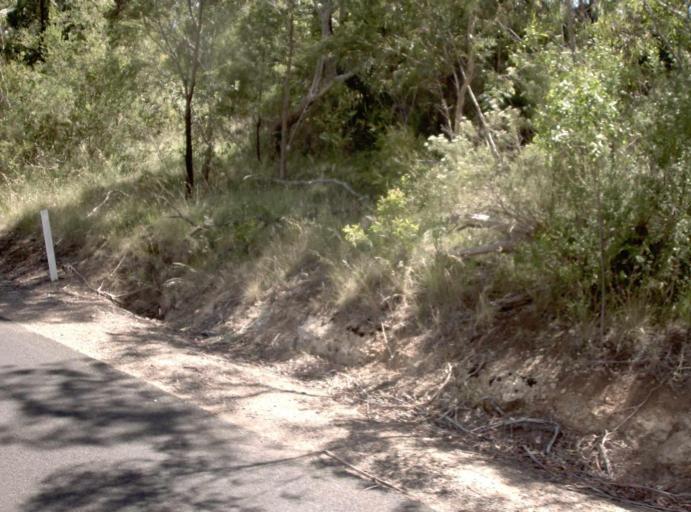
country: AU
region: Victoria
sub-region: East Gippsland
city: Lakes Entrance
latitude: -37.4466
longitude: 148.1919
